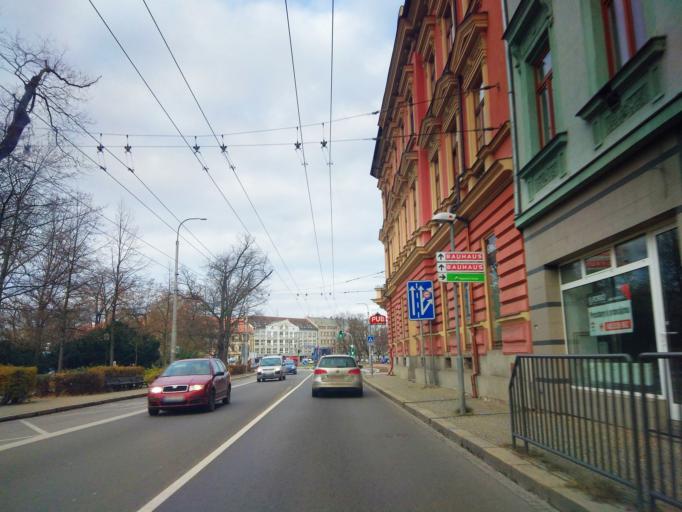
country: CZ
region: Jihocesky
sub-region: Okres Ceske Budejovice
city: Ceske Budejovice
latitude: 48.9780
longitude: 14.4754
